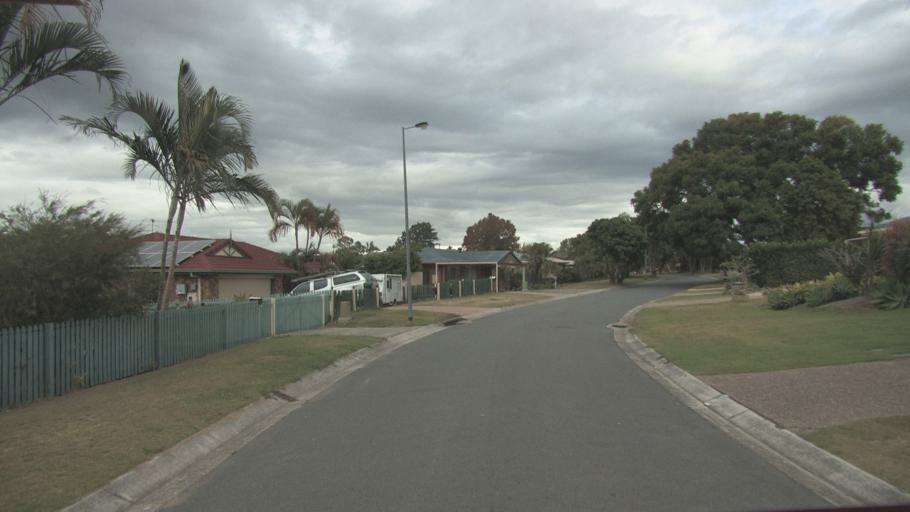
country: AU
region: Queensland
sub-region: Logan
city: Park Ridge South
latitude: -27.6796
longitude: 153.0477
